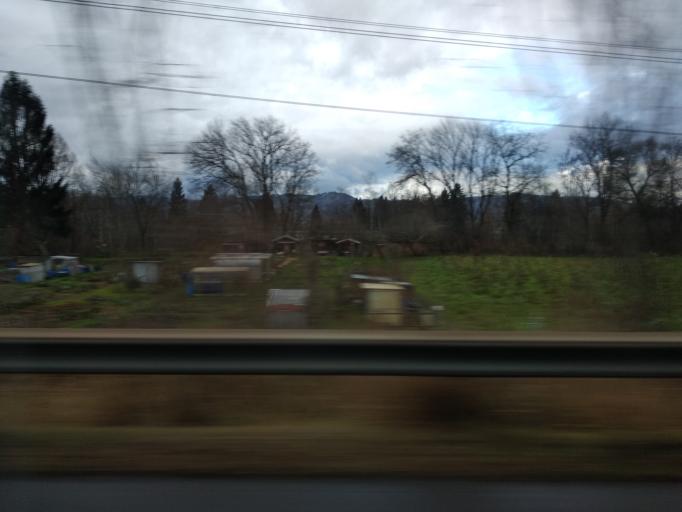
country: AT
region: Vorarlberg
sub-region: Politischer Bezirk Dornbirn
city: Hohenems
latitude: 47.3798
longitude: 9.6749
